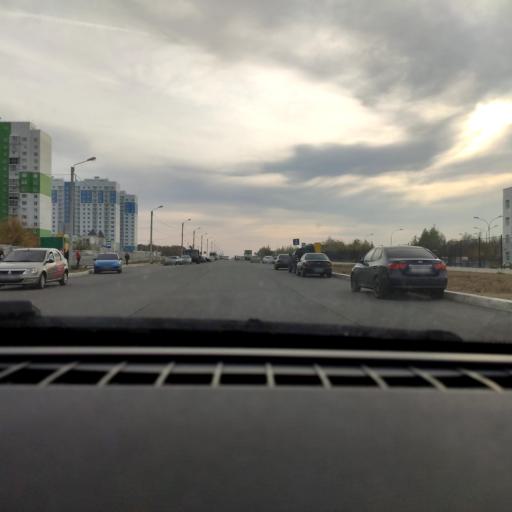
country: RU
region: Voronezj
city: Maslovka
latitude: 51.6328
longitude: 39.2936
